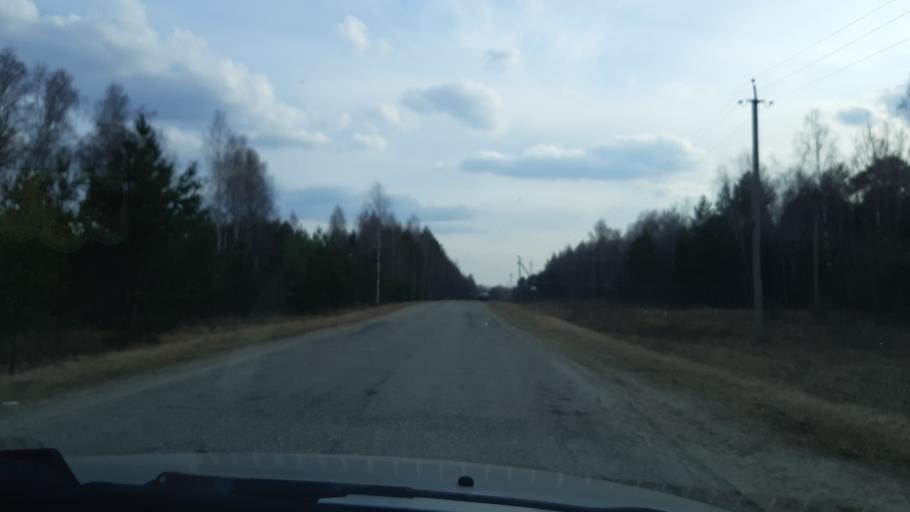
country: RU
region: Vladimir
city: Nikologory
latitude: 56.1150
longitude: 41.9848
